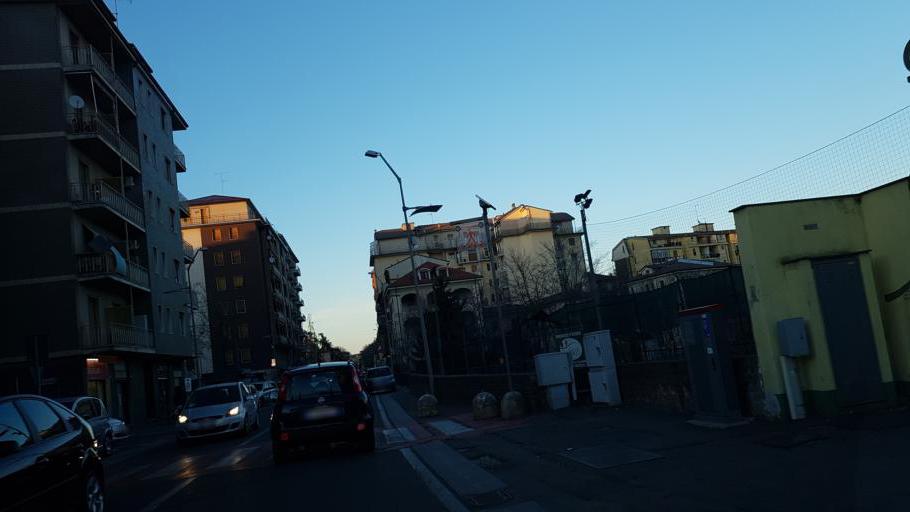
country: IT
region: Piedmont
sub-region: Provincia di Alessandria
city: Tortona
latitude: 44.8895
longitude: 8.8597
